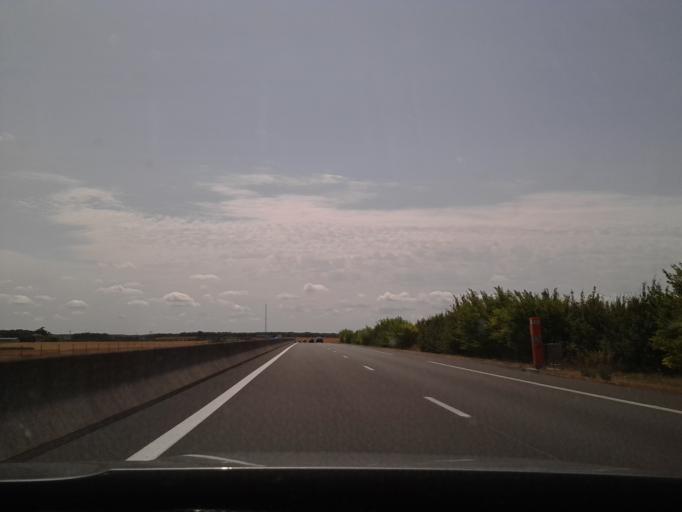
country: FR
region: Centre
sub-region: Departement d'Indre-et-Loire
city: Neuvy-le-Roi
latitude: 47.5655
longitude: 0.5884
